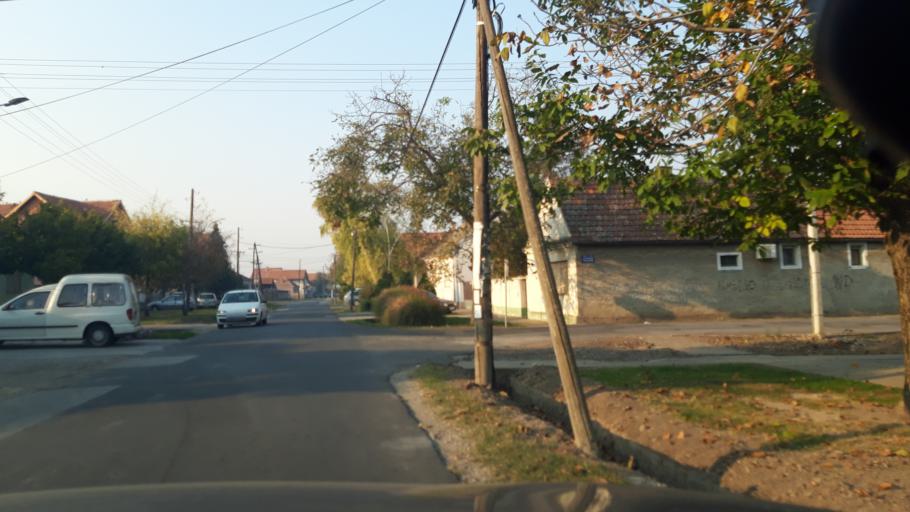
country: RS
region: Autonomna Pokrajina Vojvodina
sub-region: Sremski Okrug
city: Stara Pazova
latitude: 44.9941
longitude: 20.1462
